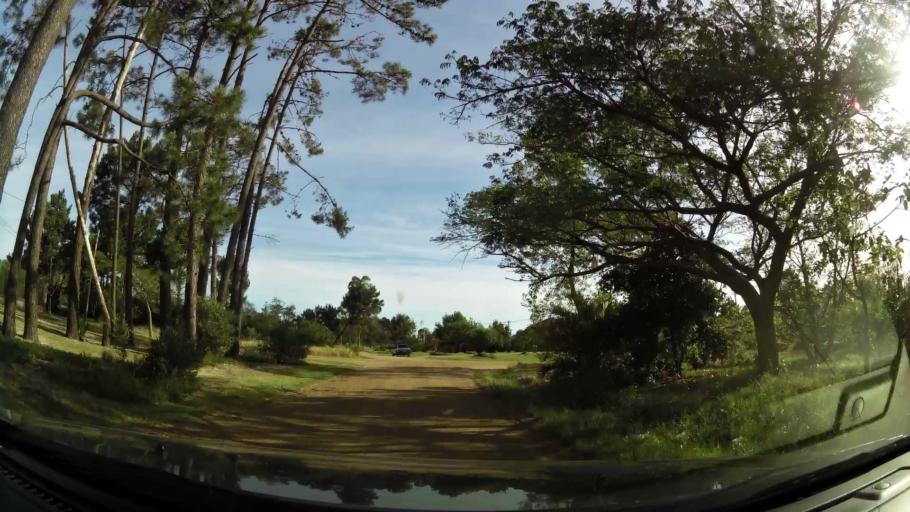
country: UY
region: Canelones
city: Empalme Olmos
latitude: -34.7836
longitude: -55.8589
